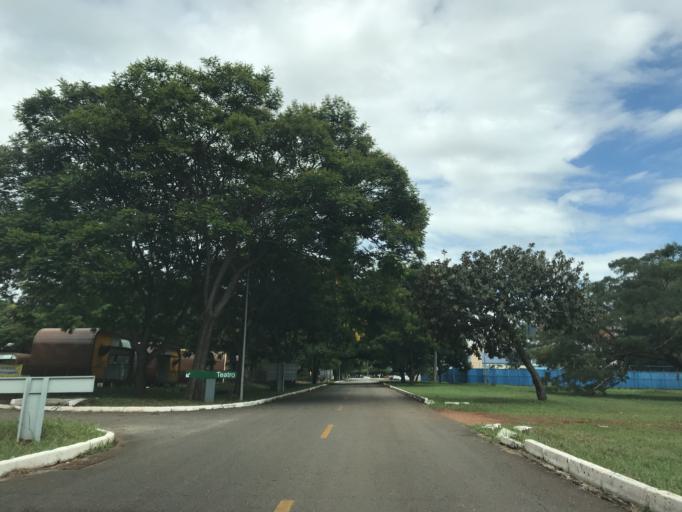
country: BR
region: Federal District
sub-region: Brasilia
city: Brasilia
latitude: -15.8088
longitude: -47.8791
